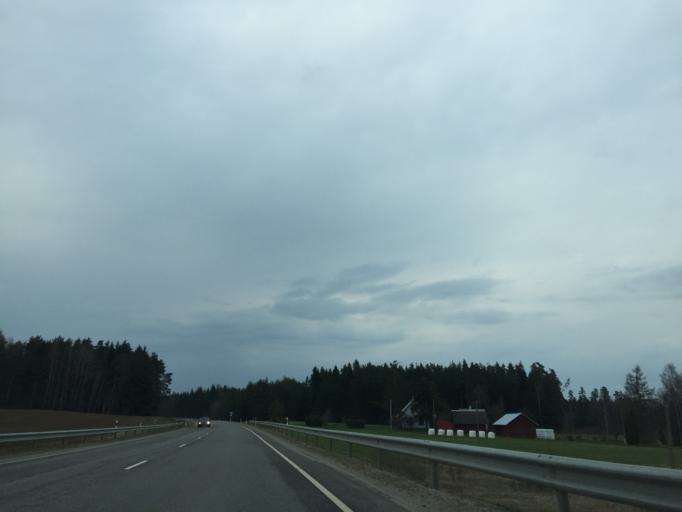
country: EE
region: Tartu
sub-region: UElenurme vald
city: Ulenurme
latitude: 58.0948
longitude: 26.7381
